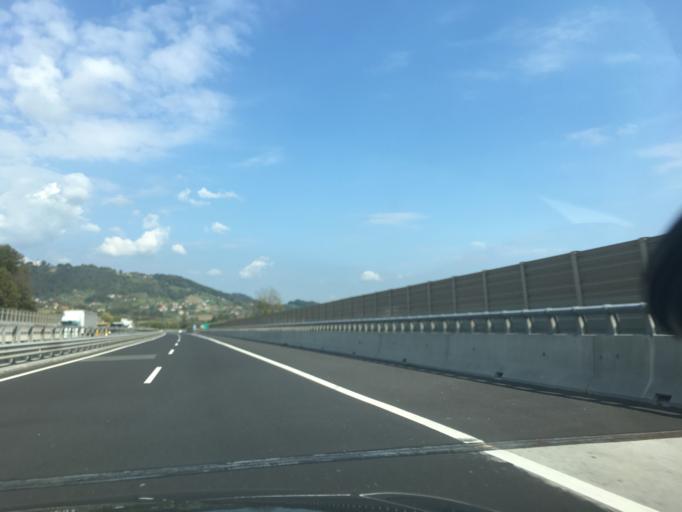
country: SI
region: Skocjan
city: Skocjan
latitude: 45.8570
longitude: 15.2537
